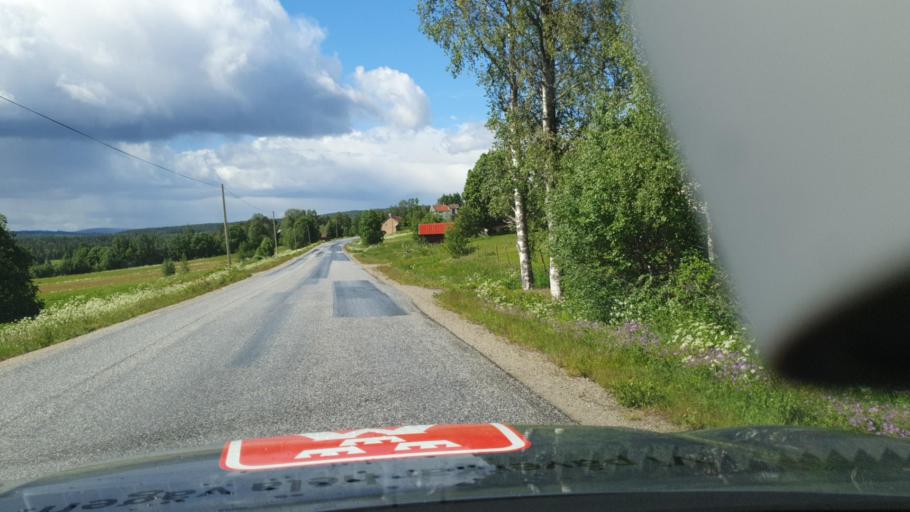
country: SE
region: Vaesternorrland
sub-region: OErnskoeldsviks Kommun
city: Bredbyn
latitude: 63.3315
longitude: 18.0441
